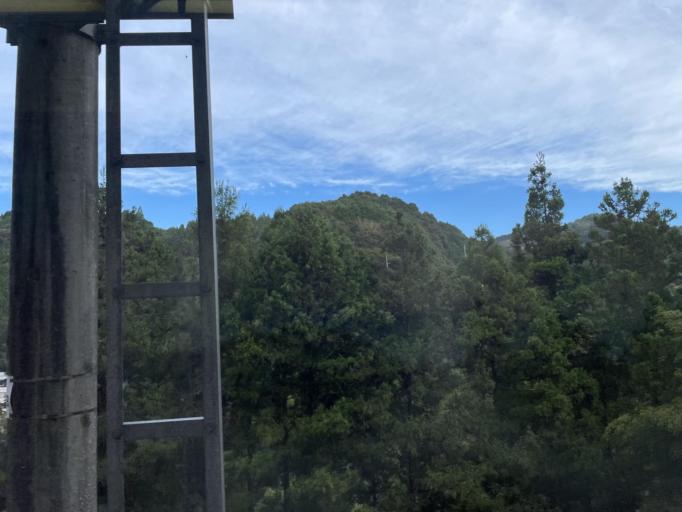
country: JP
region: Wakayama
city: Hashimoto
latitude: 34.2661
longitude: 135.5519
